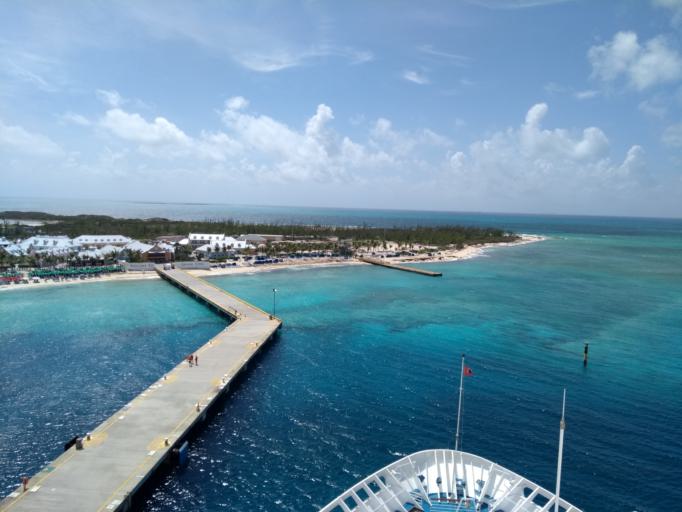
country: TC
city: Cockburn Town
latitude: 21.4279
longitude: -71.1475
